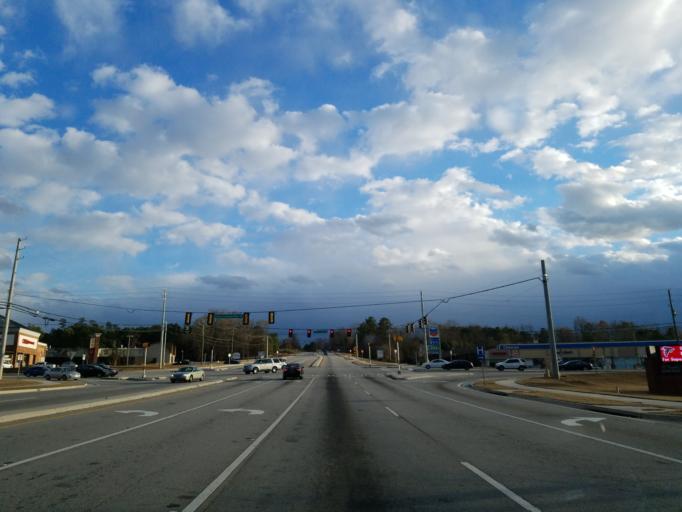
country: US
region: Georgia
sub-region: Henry County
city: Stockbridge
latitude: 33.5191
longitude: -84.1915
